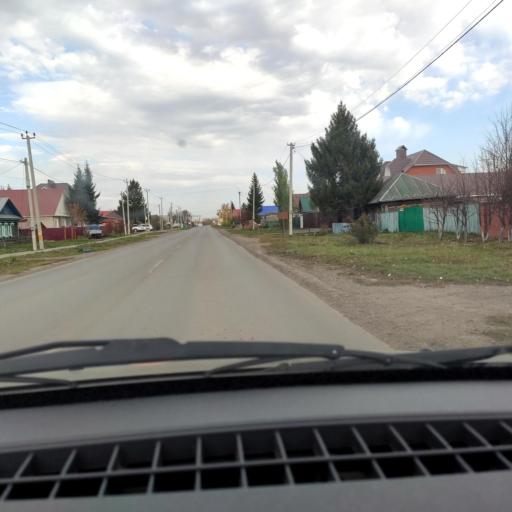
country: RU
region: Bashkortostan
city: Ufa
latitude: 54.6175
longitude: 55.9044
